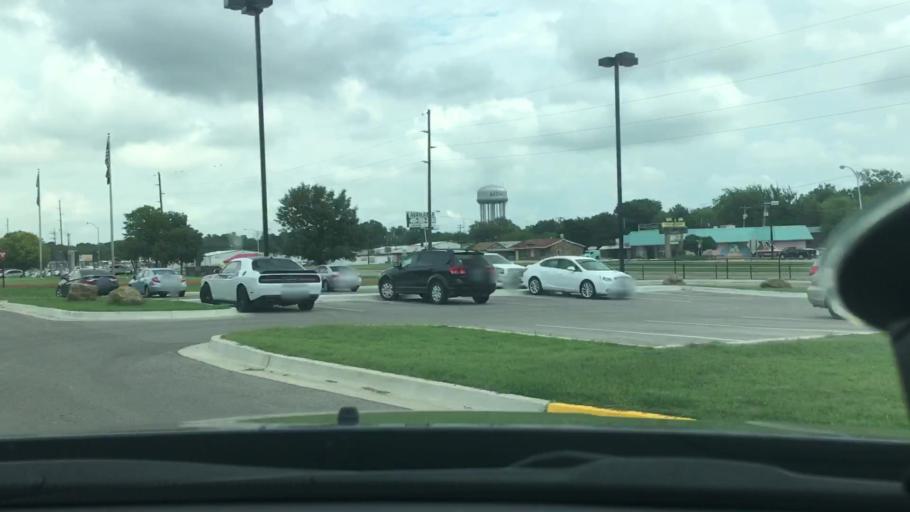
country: US
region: Oklahoma
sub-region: Carter County
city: Ardmore
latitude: 34.1599
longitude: -97.1442
